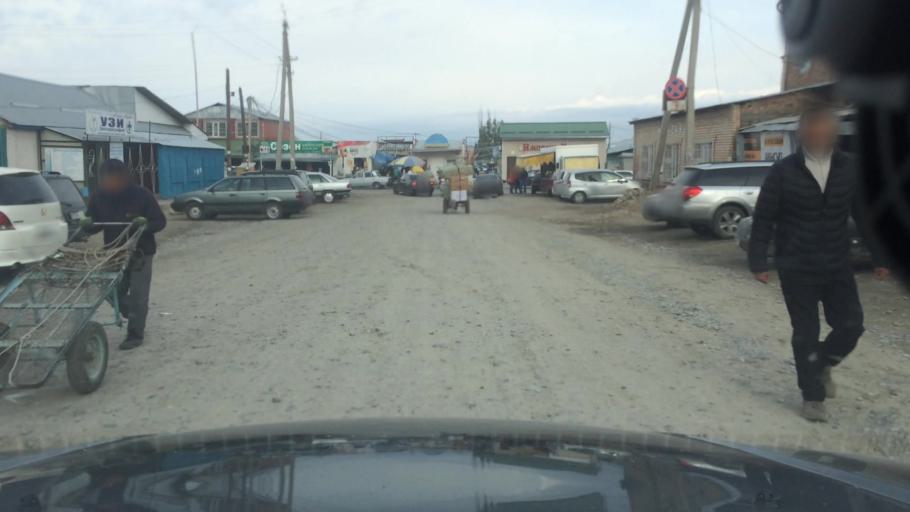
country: KG
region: Ysyk-Koel
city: Karakol
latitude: 42.4917
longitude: 78.3860
